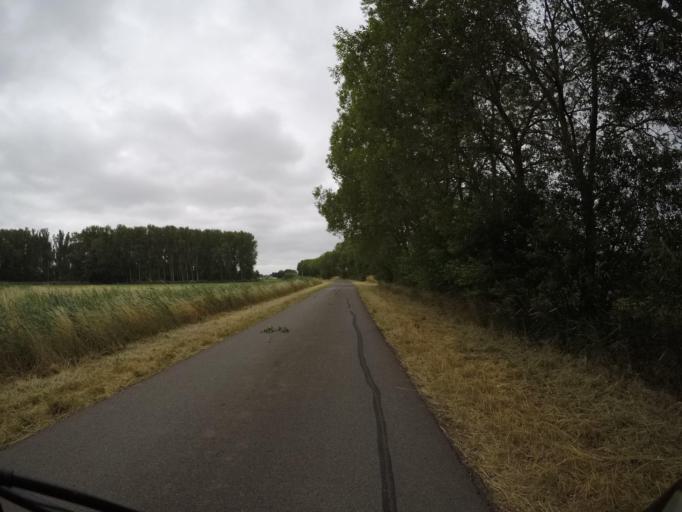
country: DE
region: Lower Saxony
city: Hitzacker
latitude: 53.1603
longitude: 11.0880
